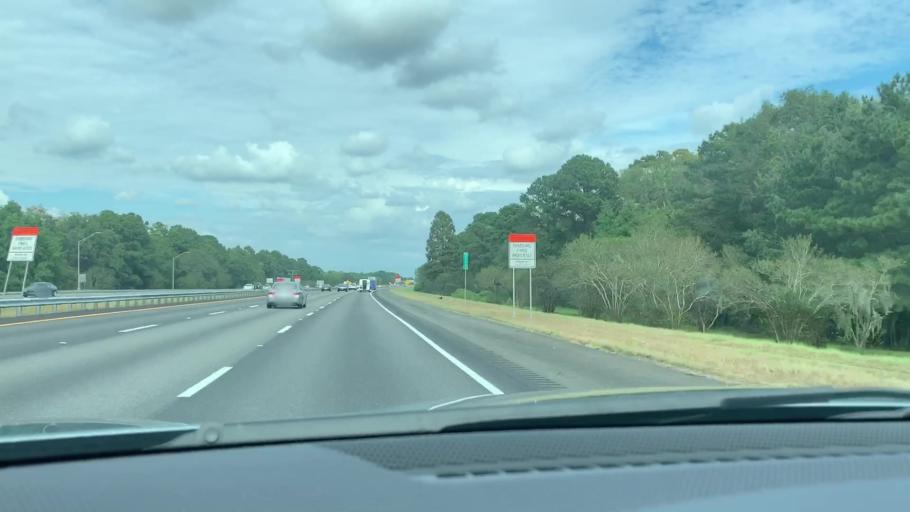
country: US
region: Georgia
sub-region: Chatham County
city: Port Wentworth
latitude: 32.2234
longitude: -81.1673
